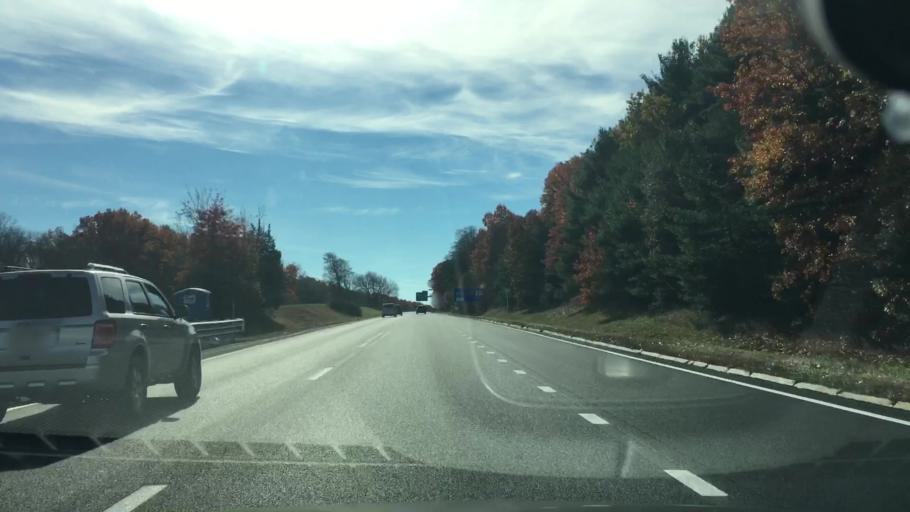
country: US
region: Massachusetts
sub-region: Hampshire County
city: Northampton
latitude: 42.3599
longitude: -72.6372
